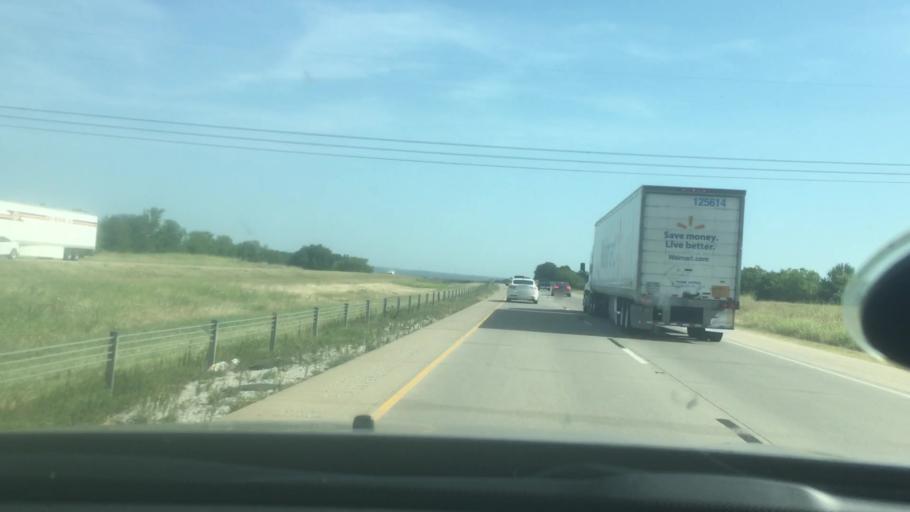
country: US
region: Oklahoma
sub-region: Carter County
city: Ardmore
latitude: 34.2307
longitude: -97.1615
